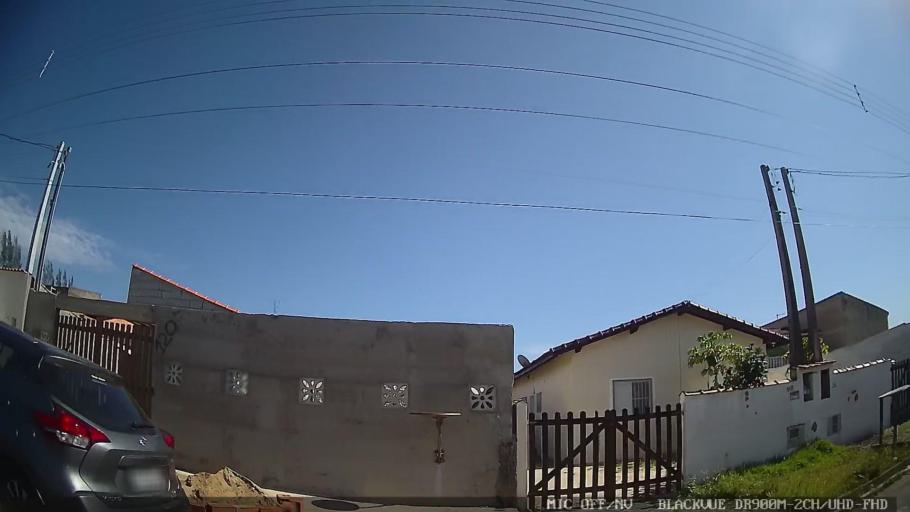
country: BR
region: Sao Paulo
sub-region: Itanhaem
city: Itanhaem
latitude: -24.2162
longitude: -46.8566
